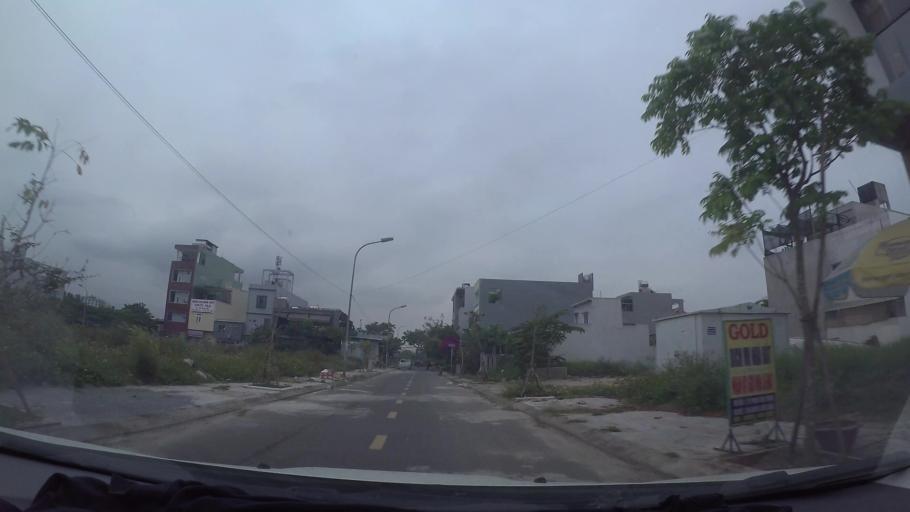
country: VN
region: Da Nang
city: Lien Chieu
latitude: 16.0759
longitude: 108.1607
